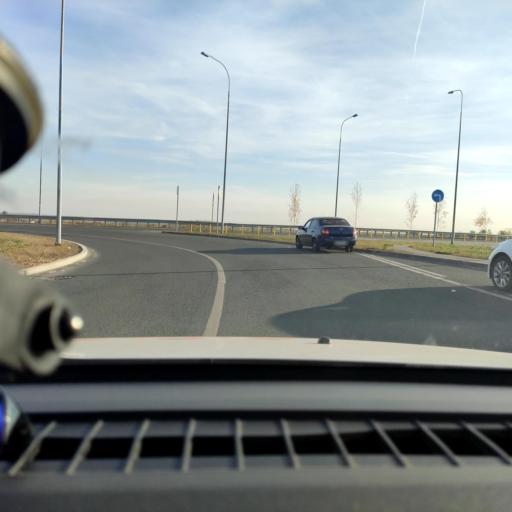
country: RU
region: Samara
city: Bereza
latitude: 53.5151
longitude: 50.1556
